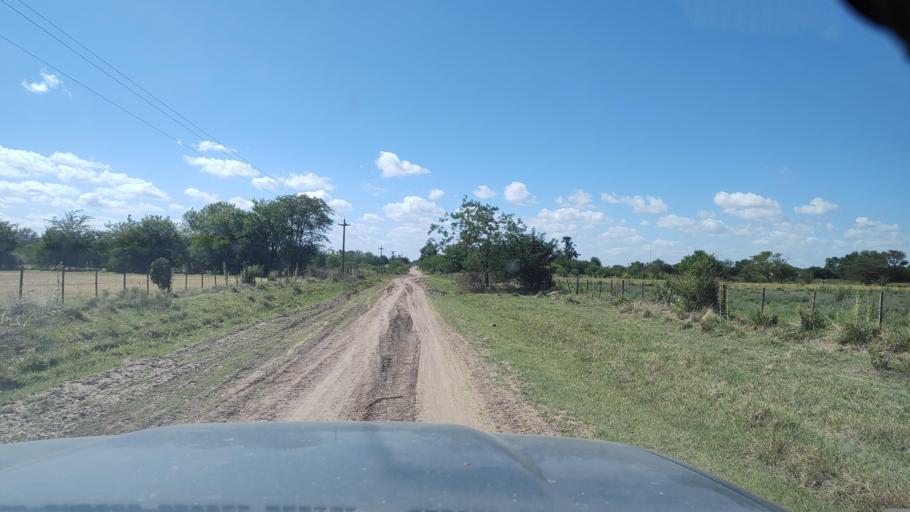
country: AR
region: Buenos Aires
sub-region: Partido de Lujan
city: Lujan
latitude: -34.5203
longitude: -59.1592
